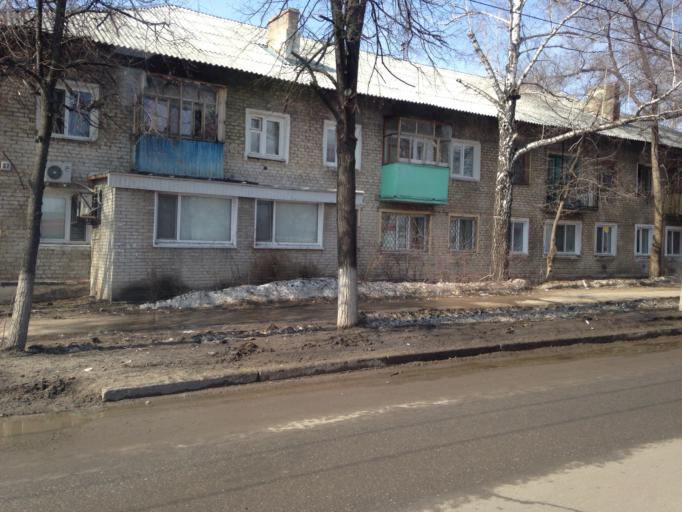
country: RU
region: Ulyanovsk
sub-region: Ulyanovskiy Rayon
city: Ulyanovsk
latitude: 54.3474
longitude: 48.5485
